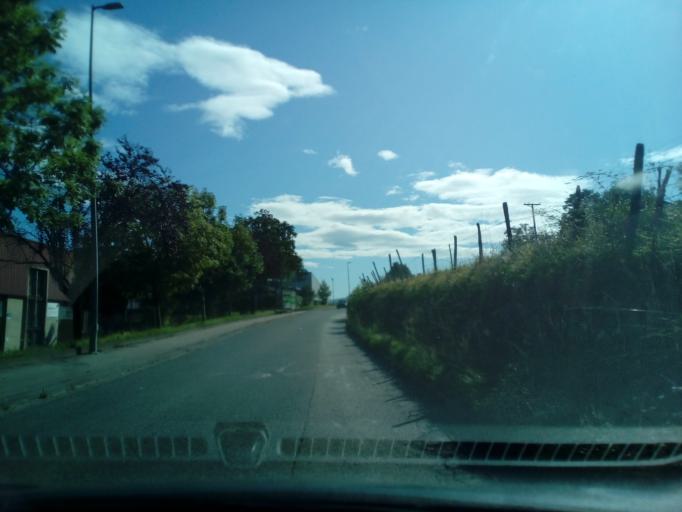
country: ES
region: Basque Country
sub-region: Provincia de Guipuzcoa
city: Aduna
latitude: 43.2030
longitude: -2.0441
